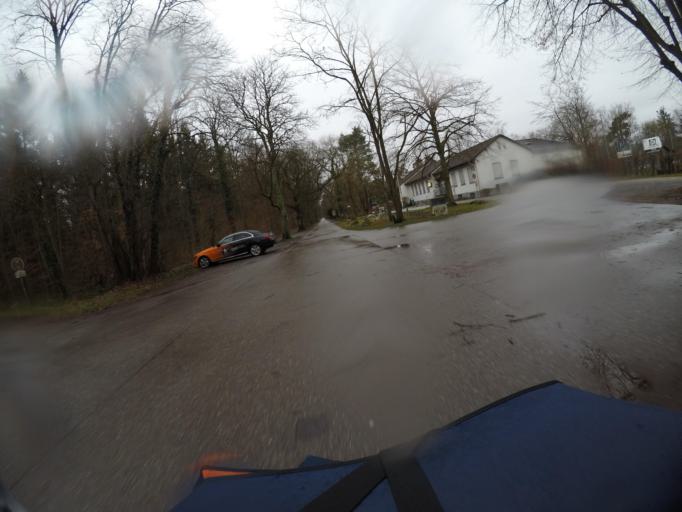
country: DE
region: Baden-Wuerttemberg
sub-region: Karlsruhe Region
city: Karlsruhe
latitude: 49.0261
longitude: 8.4136
